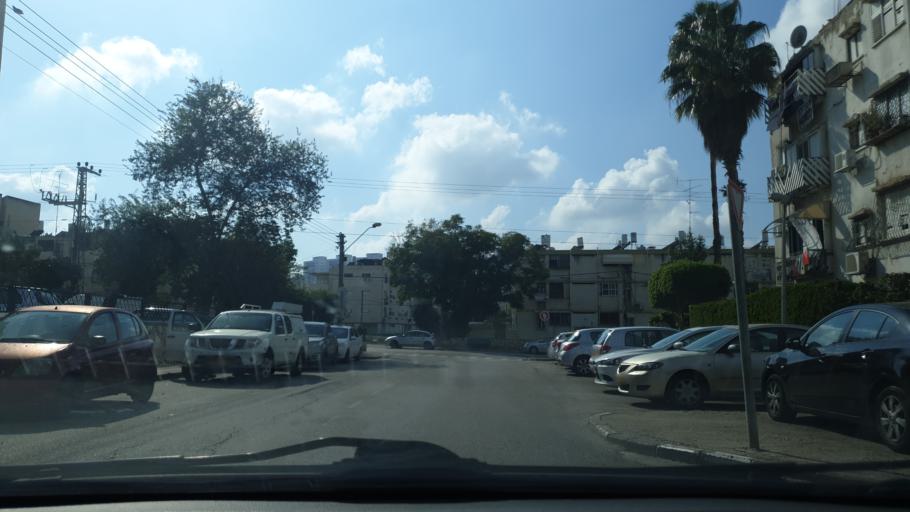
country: IL
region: Central District
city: Ramla
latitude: 31.9368
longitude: 34.8580
